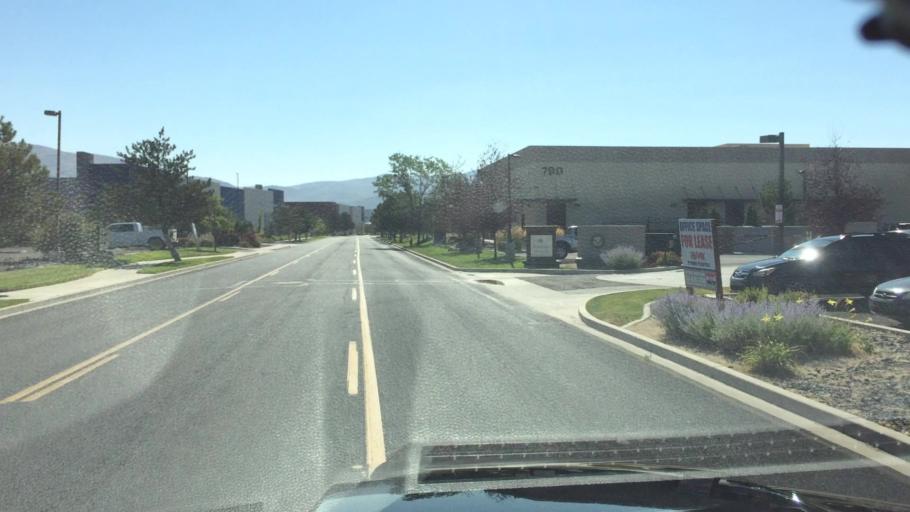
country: US
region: Nevada
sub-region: Washoe County
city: Sparks
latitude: 39.4453
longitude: -119.7597
